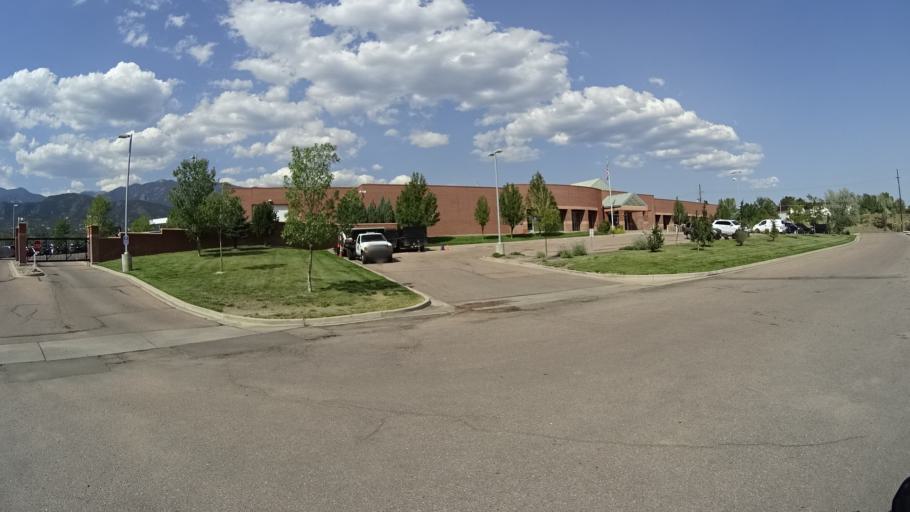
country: US
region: Colorado
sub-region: El Paso County
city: Colorado Springs
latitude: 38.8235
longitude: -104.8433
